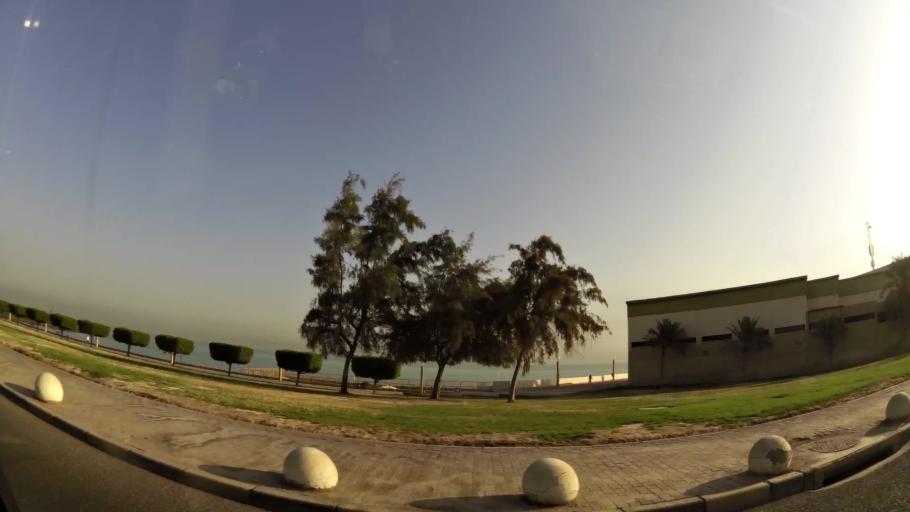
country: KW
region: Muhafazat Hawalli
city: Hawalli
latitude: 29.3452
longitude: 48.0428
